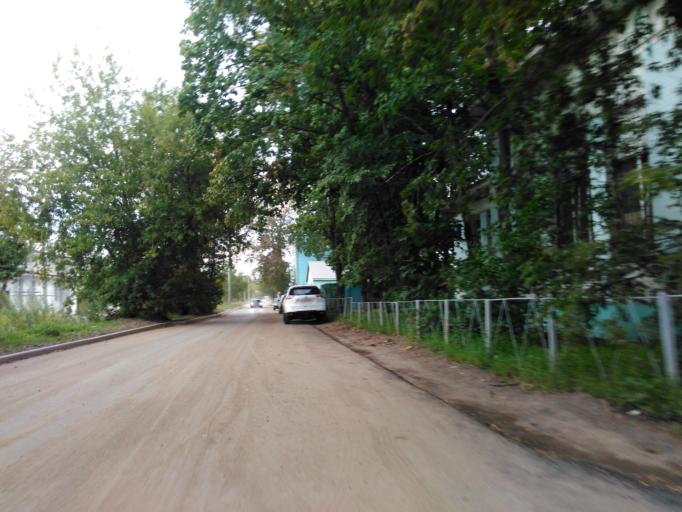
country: RU
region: Moskovskaya
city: Bogorodskoye
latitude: 55.8294
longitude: 37.7012
